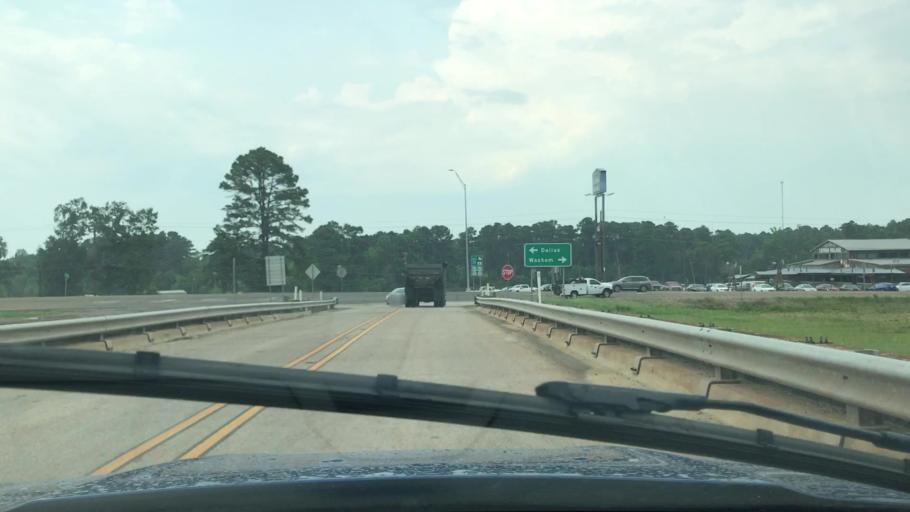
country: US
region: Texas
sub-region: Harrison County
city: Waskom
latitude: 32.4789
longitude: -94.0873
